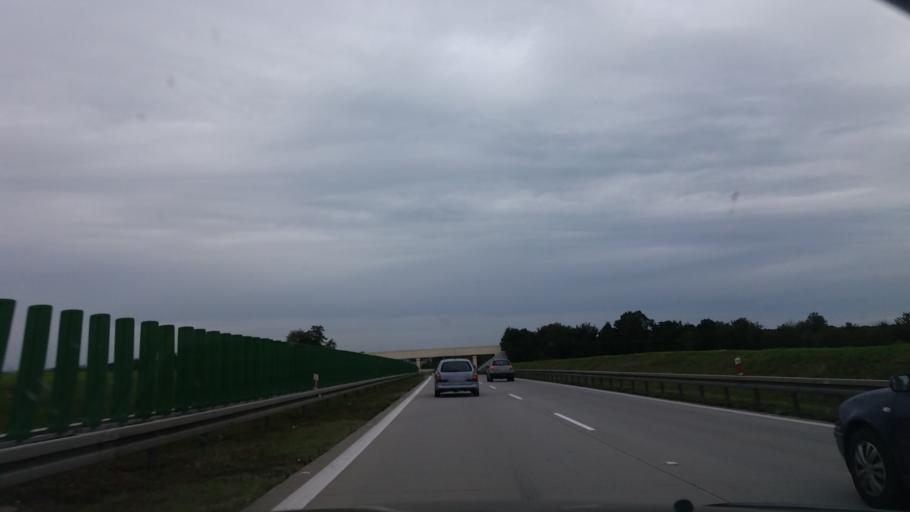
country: PL
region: Lower Silesian Voivodeship
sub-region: Powiat sredzki
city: Udanin
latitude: 51.0736
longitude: 16.4584
